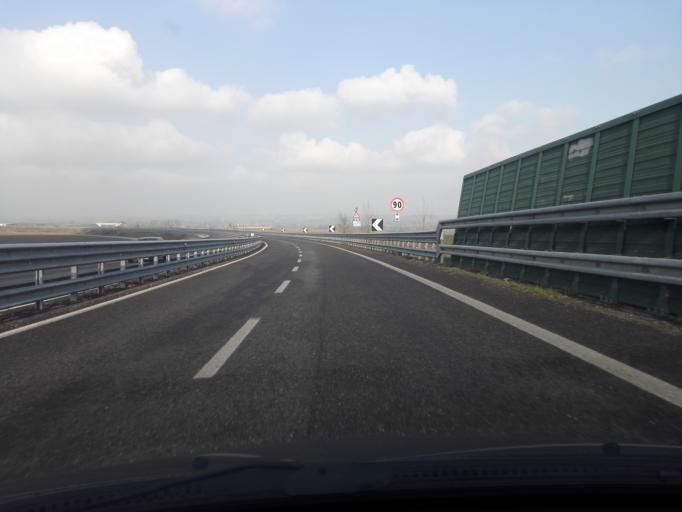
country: IT
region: Piedmont
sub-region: Provincia di Alessandria
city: Alessandria
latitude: 44.9108
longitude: 8.6425
